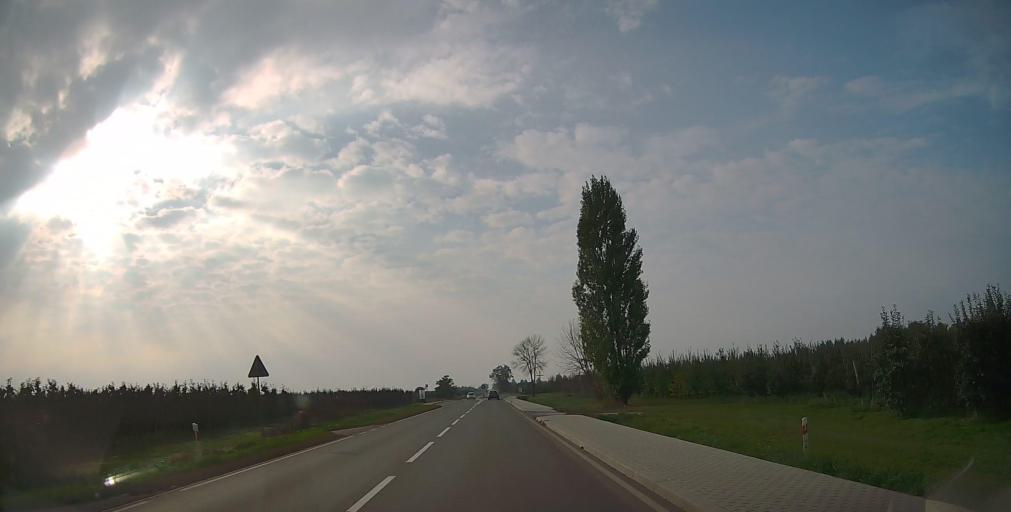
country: PL
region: Masovian Voivodeship
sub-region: Powiat grojecki
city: Bledow
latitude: 51.7651
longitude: 20.7676
